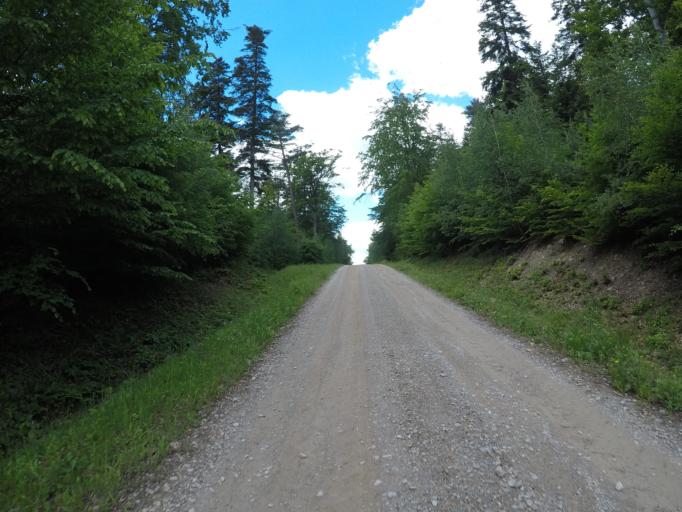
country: PL
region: Swietokrzyskie
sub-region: Powiat kielecki
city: Kostomloty Pierwsze
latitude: 50.9333
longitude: 20.6221
